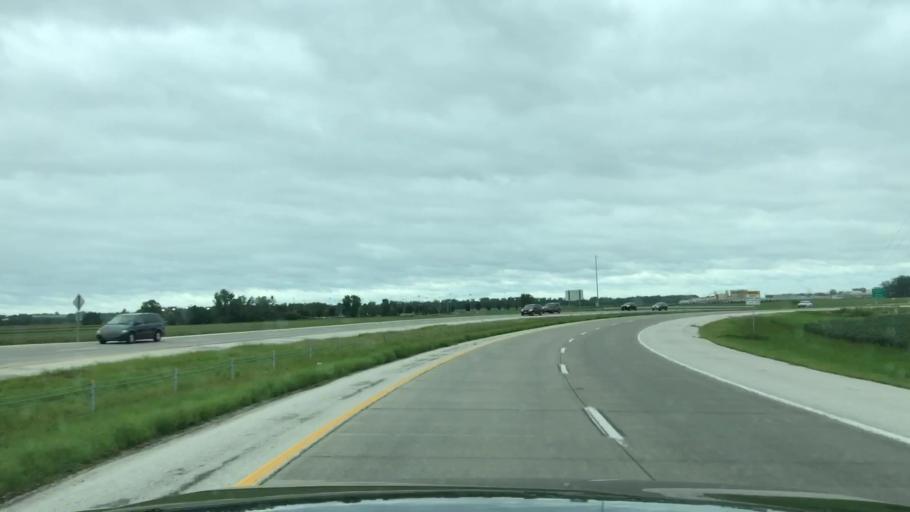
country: US
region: Missouri
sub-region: Saint Charles County
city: Saint Charles
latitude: 38.7256
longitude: -90.4985
